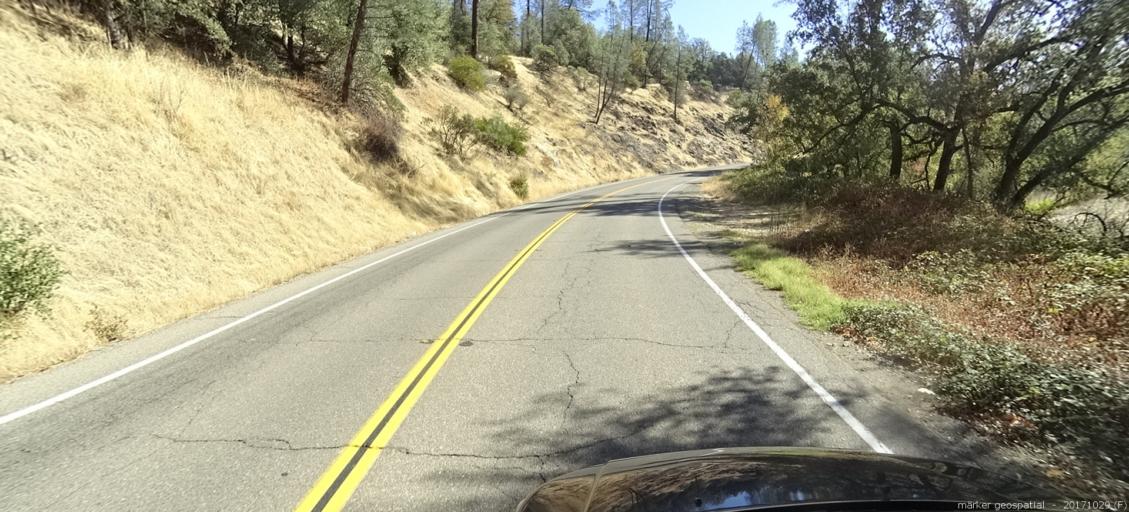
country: US
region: California
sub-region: Shasta County
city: Shasta
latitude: 40.4959
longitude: -122.4742
